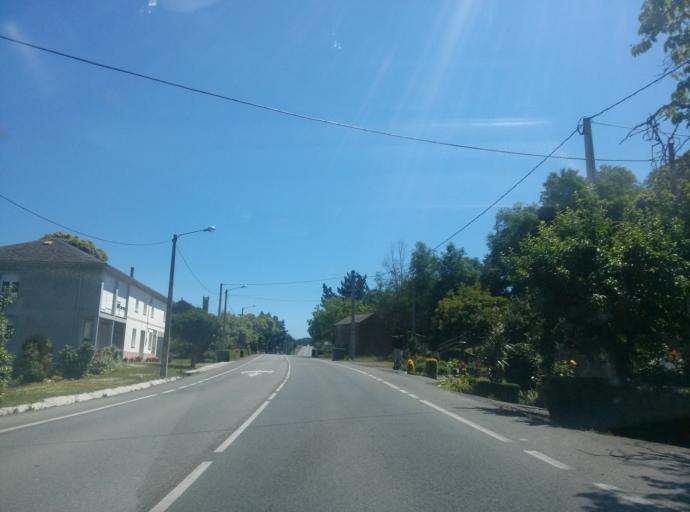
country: ES
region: Galicia
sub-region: Provincia de Lugo
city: Castro de Rei
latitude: 43.2459
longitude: -7.4129
